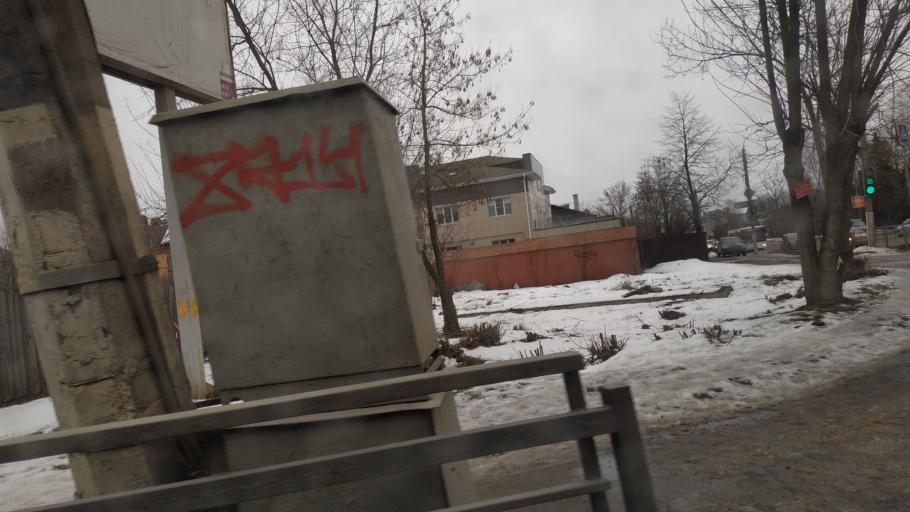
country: RU
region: Tverskaya
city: Tver
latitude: 56.8788
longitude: 35.8988
